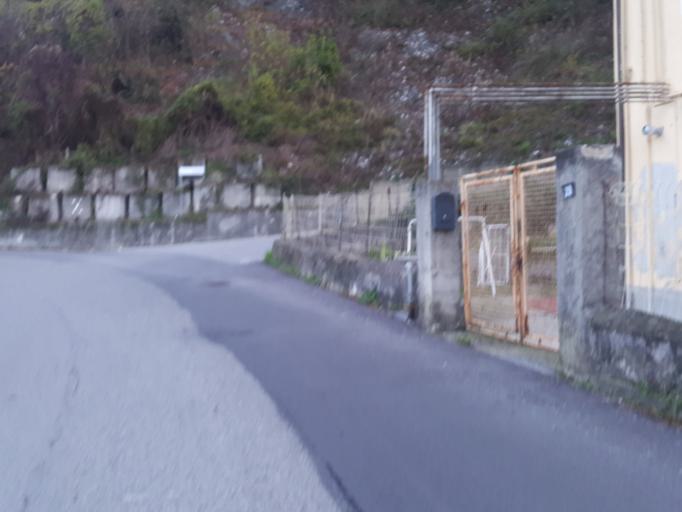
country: IT
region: Liguria
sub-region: Provincia di Genova
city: Mignanego
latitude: 44.5292
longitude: 8.9083
